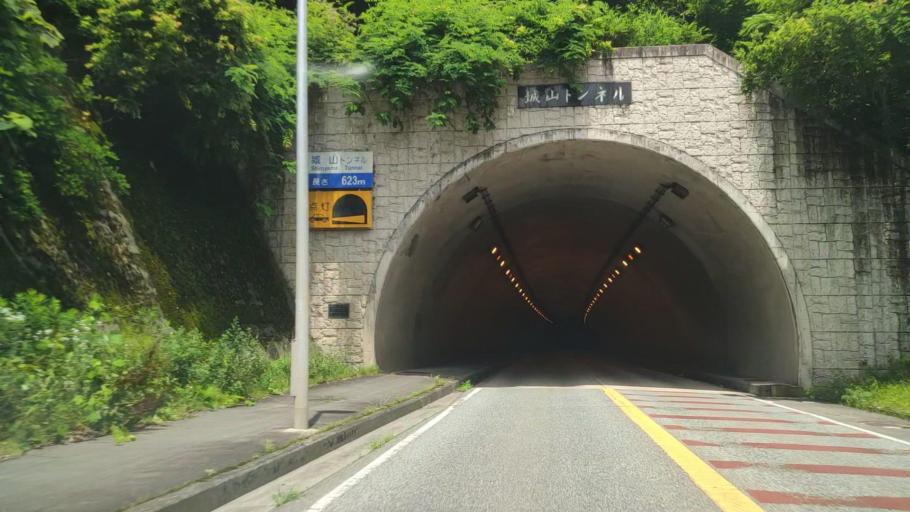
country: JP
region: Hyogo
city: Toyooka
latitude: 35.4590
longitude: 134.7686
